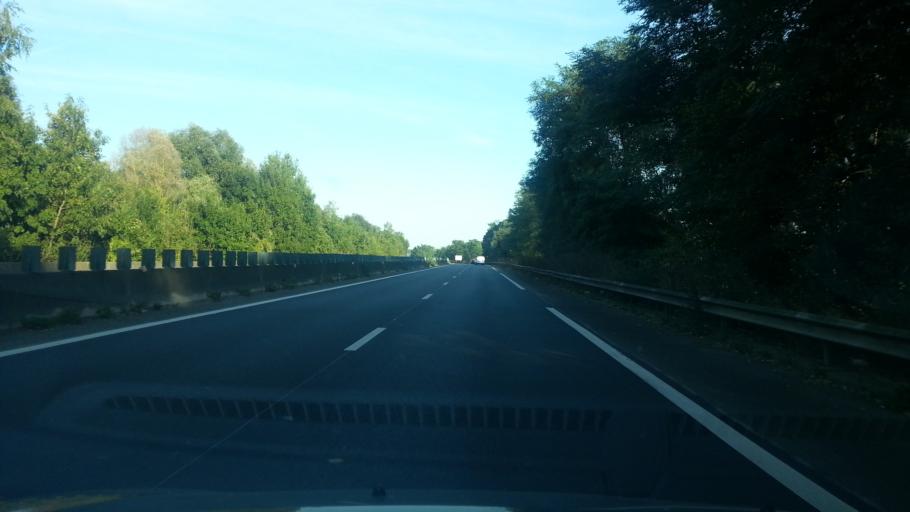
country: FR
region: Picardie
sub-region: Departement de l'Oise
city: Clermont
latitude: 49.3896
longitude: 2.4001
